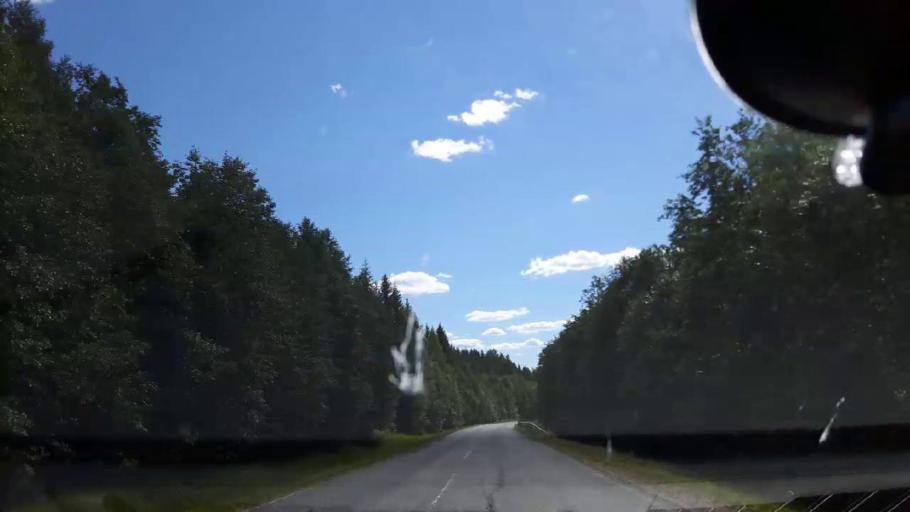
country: SE
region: Vaesternorrland
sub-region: Ange Kommun
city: Fransta
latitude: 62.8107
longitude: 16.2121
